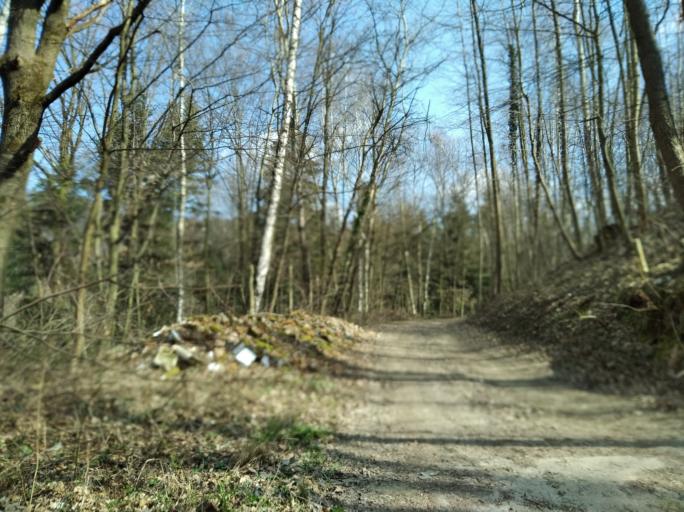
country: PL
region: Subcarpathian Voivodeship
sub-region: Powiat strzyzowski
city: Jawornik
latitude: 49.8437
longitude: 21.8406
